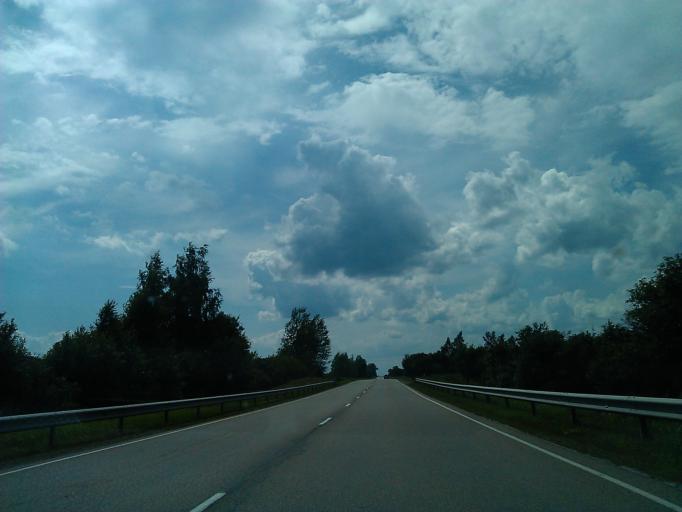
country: LV
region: Jaunpils
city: Jaunpils
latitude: 56.6672
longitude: 23.0605
